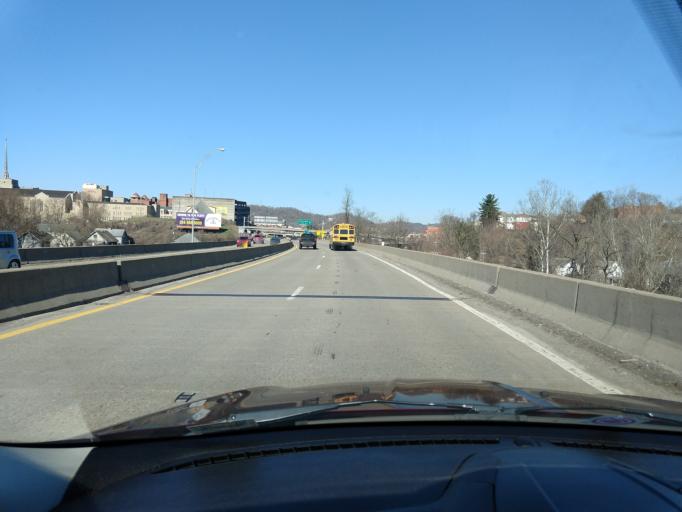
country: US
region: West Virginia
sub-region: Harrison County
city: Clarksburg
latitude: 39.2810
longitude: -80.3337
